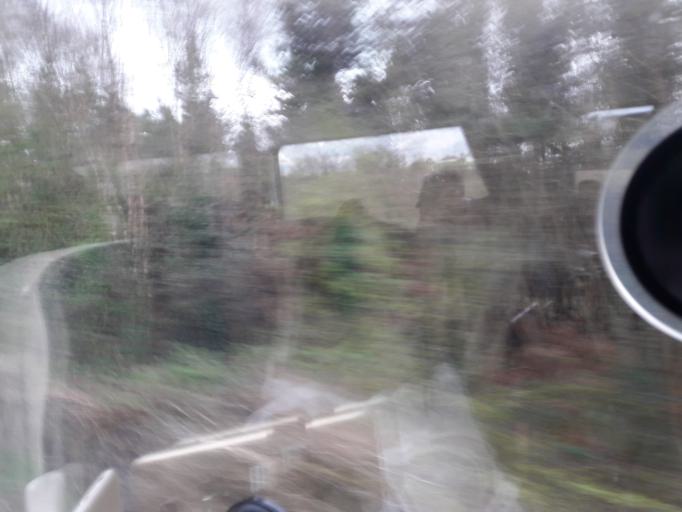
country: IE
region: Leinster
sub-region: An Iarmhi
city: Rathwire
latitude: 53.4954
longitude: -7.2336
